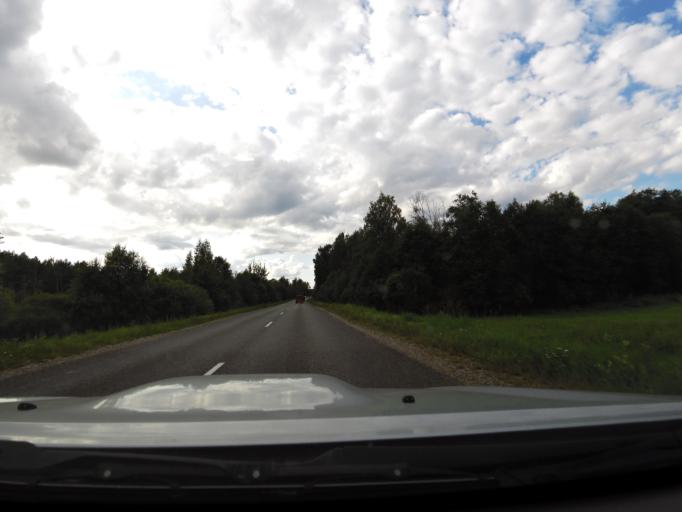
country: LV
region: Akniste
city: Akniste
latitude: 56.0100
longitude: 25.9349
